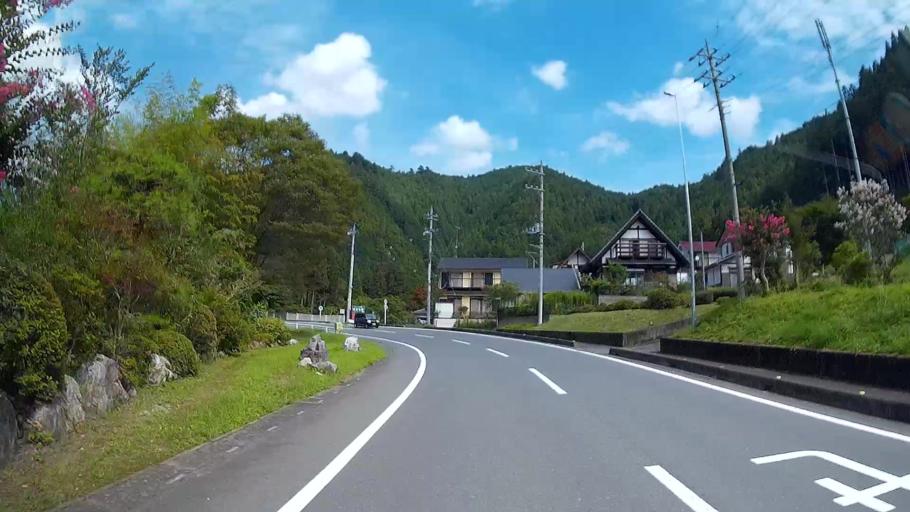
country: JP
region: Saitama
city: Chichibu
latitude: 35.8985
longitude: 139.1695
